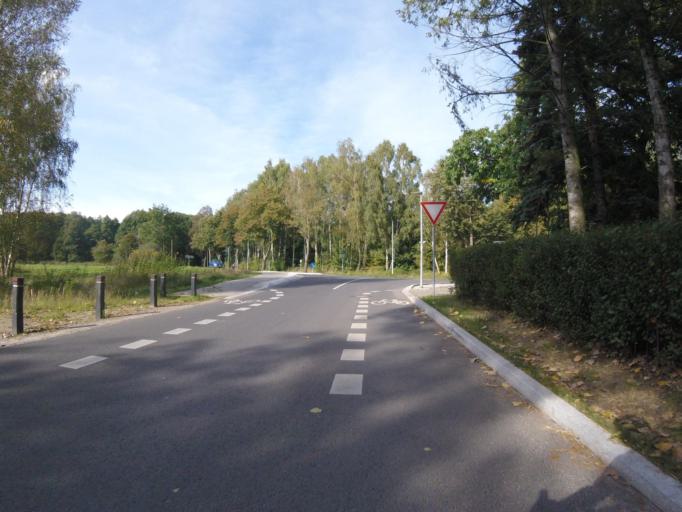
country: DE
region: Brandenburg
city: Konigs Wusterhausen
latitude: 52.2852
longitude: 13.6537
